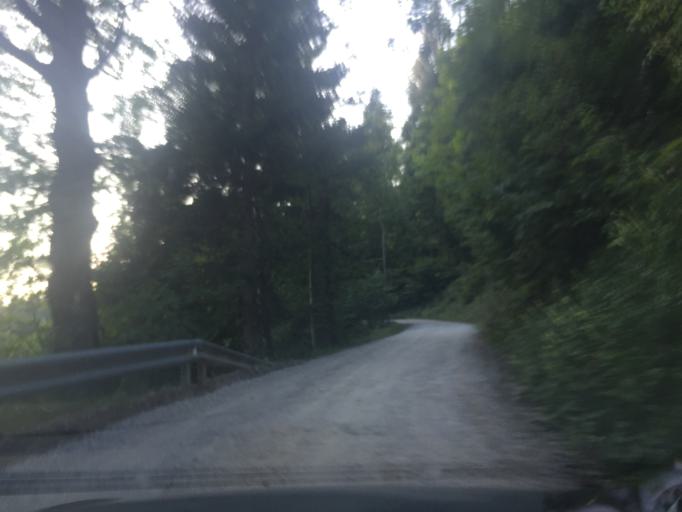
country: SI
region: Sostanj
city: Topolsica
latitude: 46.4541
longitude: 14.9906
